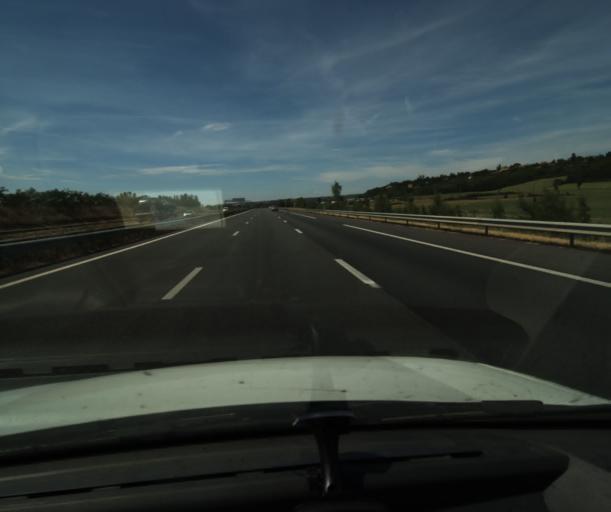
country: FR
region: Midi-Pyrenees
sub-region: Departement de la Haute-Garonne
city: Saint-Sauveur
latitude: 43.7373
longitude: 1.3940
